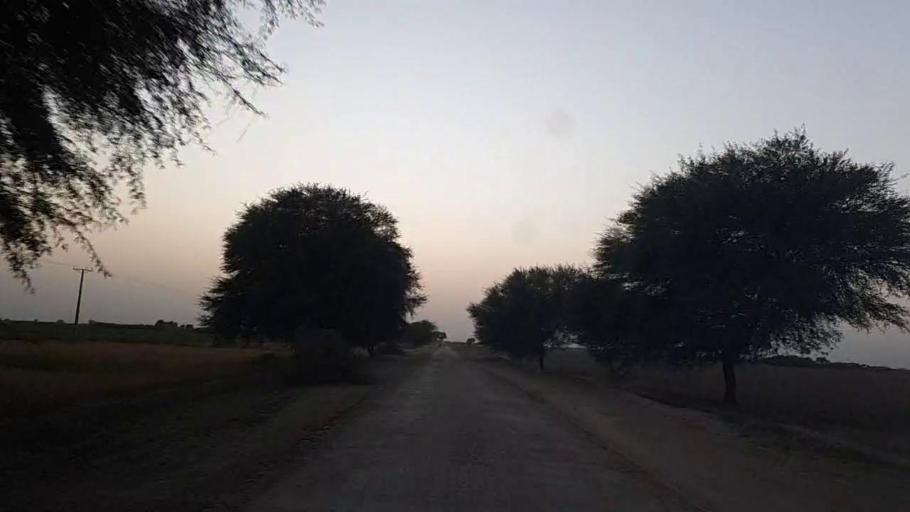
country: PK
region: Sindh
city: Naukot
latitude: 24.7530
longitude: 69.2943
